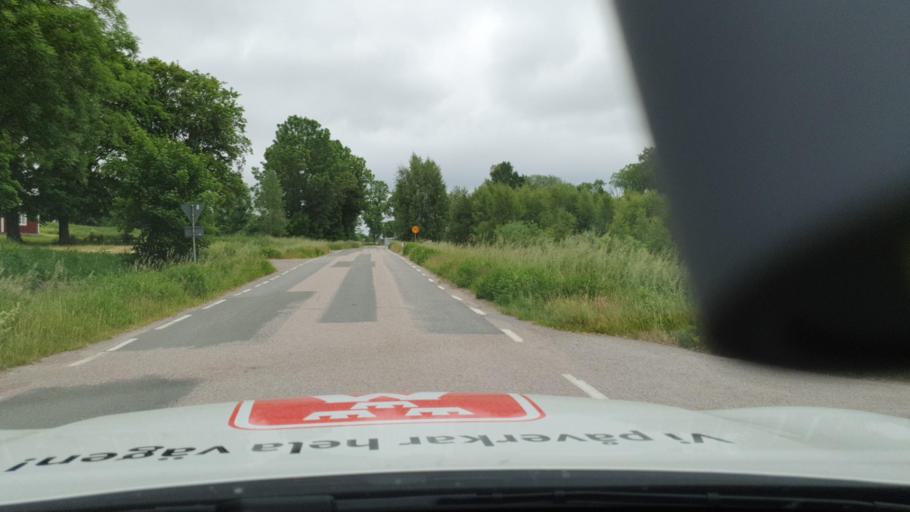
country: SE
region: Vaestra Goetaland
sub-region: Tibro Kommun
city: Tibro
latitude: 58.3424
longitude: 14.1954
